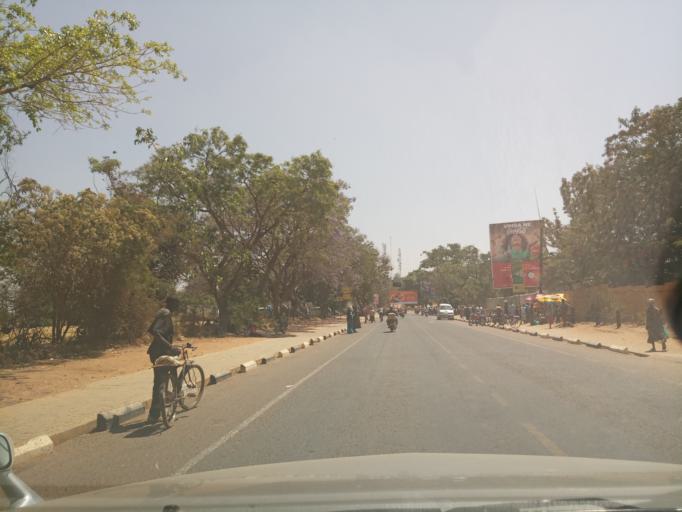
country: UG
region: Northern Region
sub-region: Arua District
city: Arua
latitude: 3.0160
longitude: 30.9139
